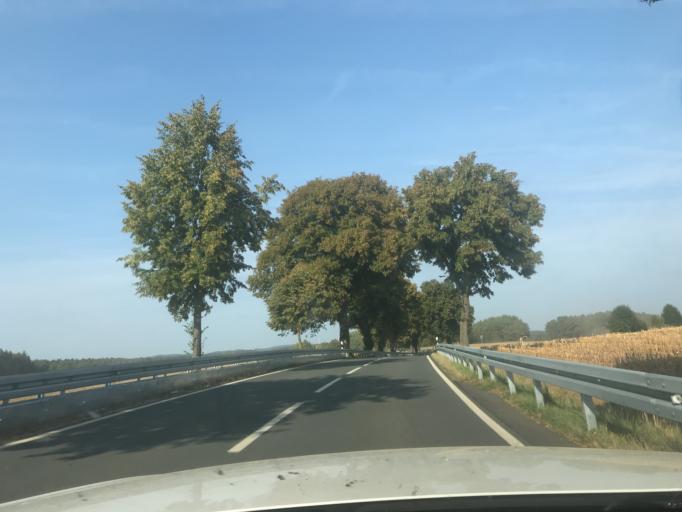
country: DE
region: Bavaria
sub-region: Upper Franconia
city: Pottenstein
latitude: 49.7143
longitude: 11.4443
